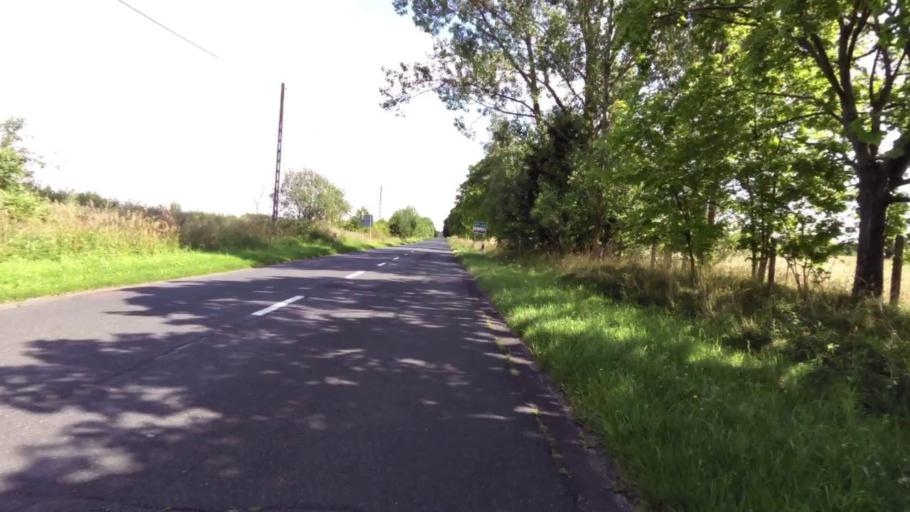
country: PL
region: West Pomeranian Voivodeship
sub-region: Powiat stargardzki
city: Dobrzany
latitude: 53.3701
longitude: 15.4319
